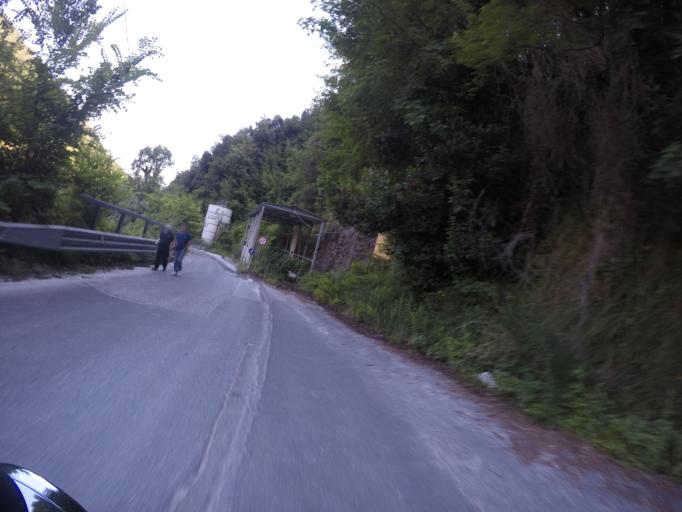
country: IT
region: Tuscany
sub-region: Provincia di Massa-Carrara
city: Carrara
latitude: 44.0926
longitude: 10.1019
